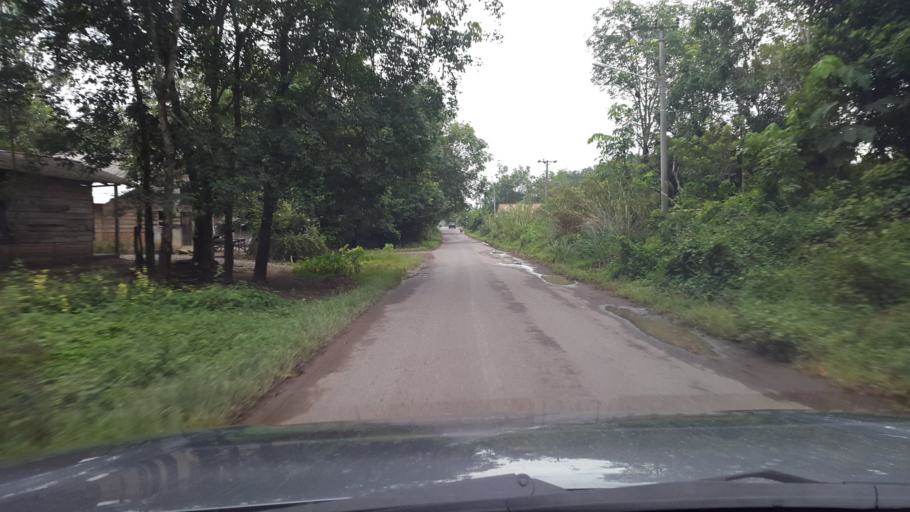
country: ID
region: South Sumatra
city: Gunungmenang
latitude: -3.2697
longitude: 104.0542
